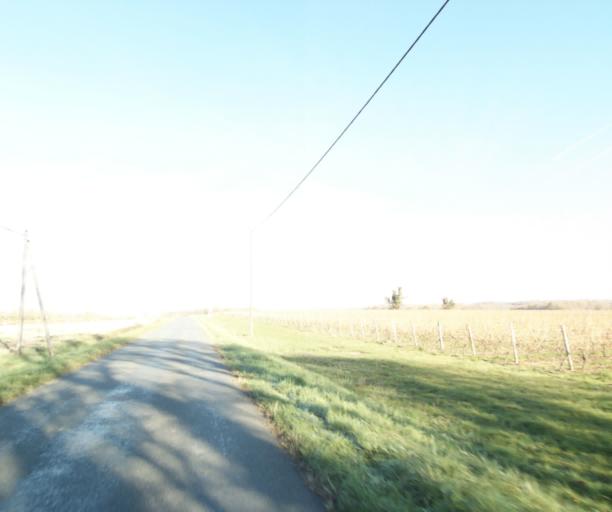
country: FR
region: Poitou-Charentes
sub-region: Departement de la Charente-Maritime
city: Cherac
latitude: 45.7168
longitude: -0.4530
